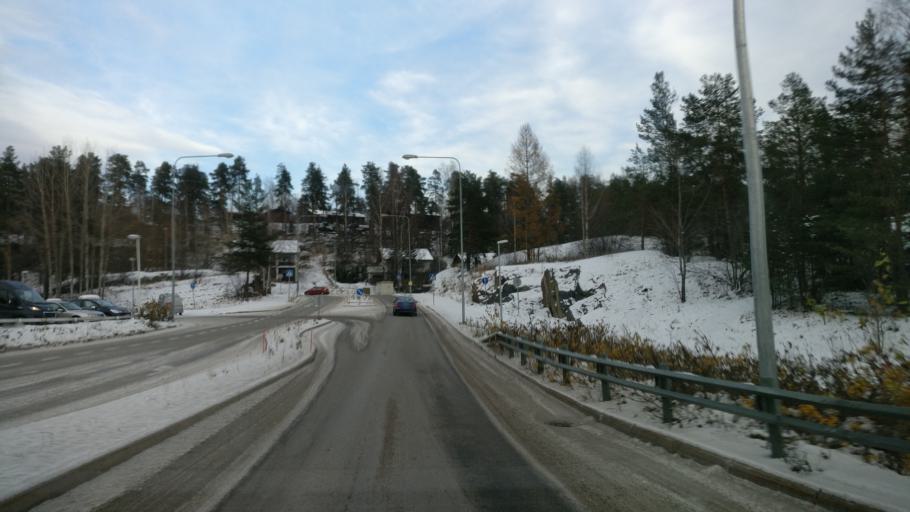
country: FI
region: Southern Savonia
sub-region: Savonlinna
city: Savonlinna
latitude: 61.8687
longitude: 28.9239
